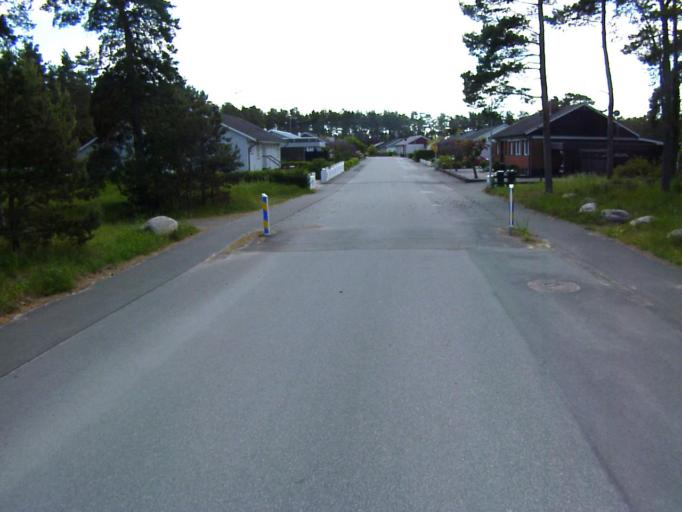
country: SE
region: Skane
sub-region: Kristianstads Kommun
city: Ahus
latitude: 55.9459
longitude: 14.2750
